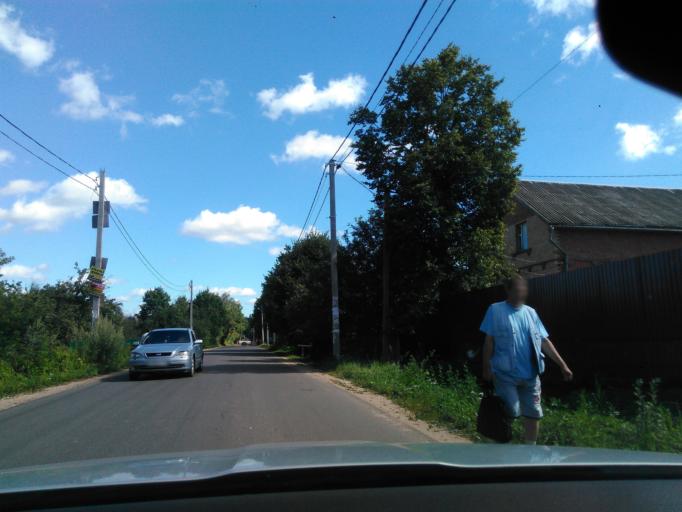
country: RU
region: Moskovskaya
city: Klin
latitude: 56.2336
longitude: 36.8218
